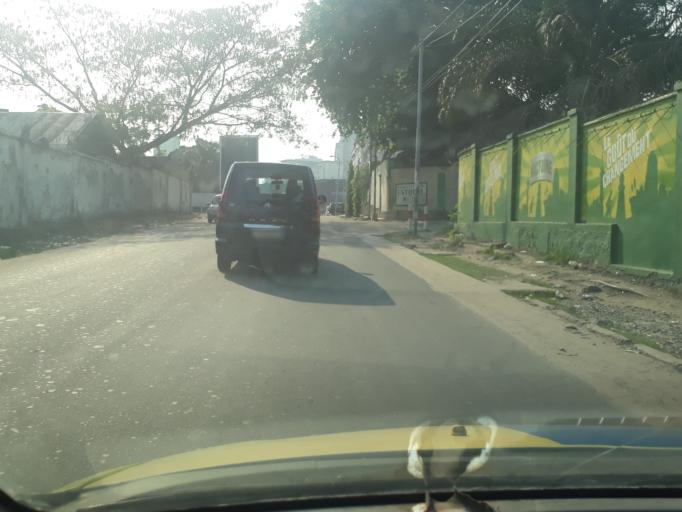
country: CD
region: Kinshasa
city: Kinshasa
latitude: -4.3047
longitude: 15.3199
